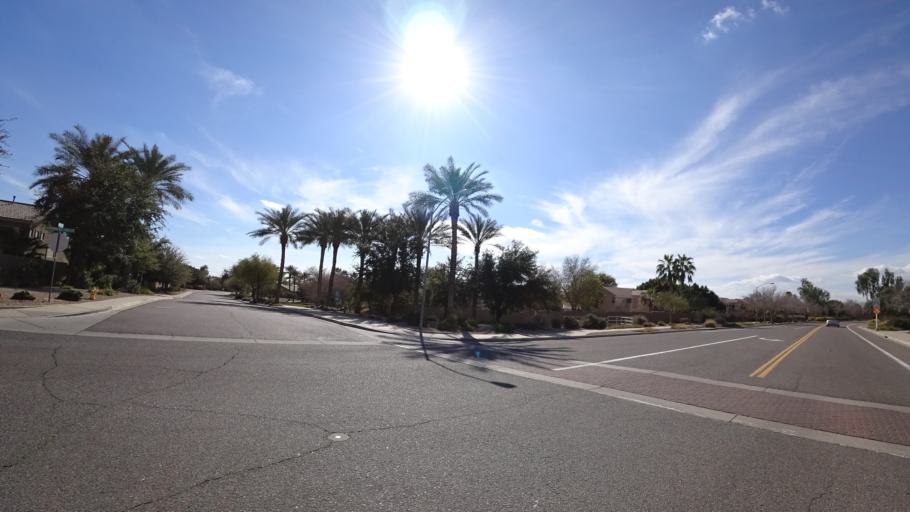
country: US
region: Arizona
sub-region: Maricopa County
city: Peoria
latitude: 33.6720
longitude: -112.2070
